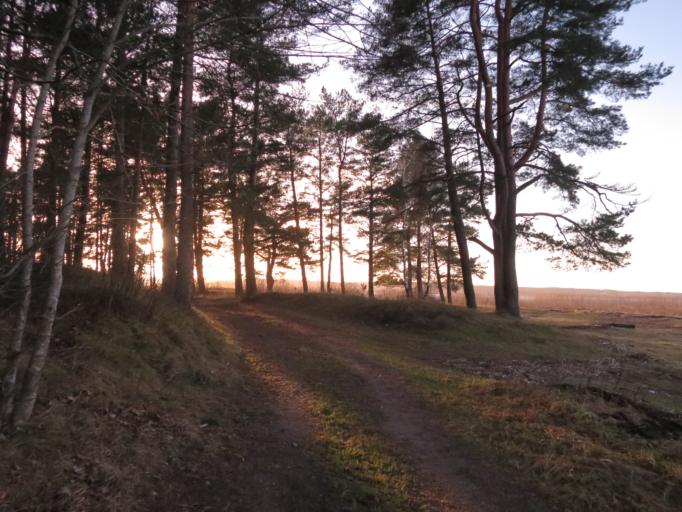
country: LV
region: Riga
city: Bergi
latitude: 56.9750
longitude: 24.3059
